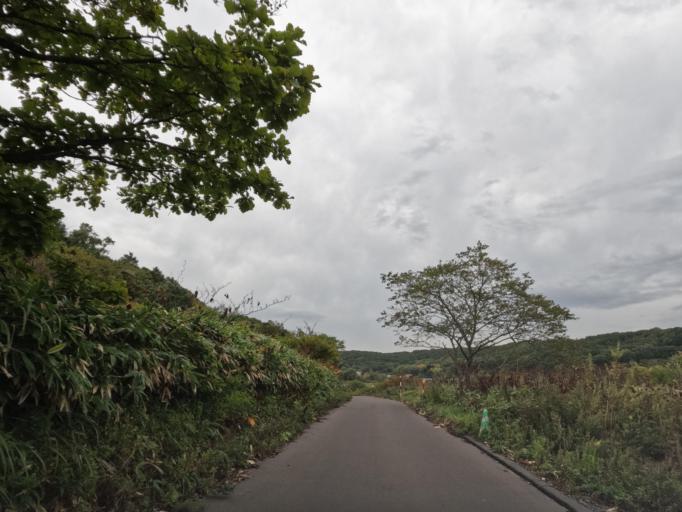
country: JP
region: Hokkaido
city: Date
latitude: 42.4001
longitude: 140.9121
